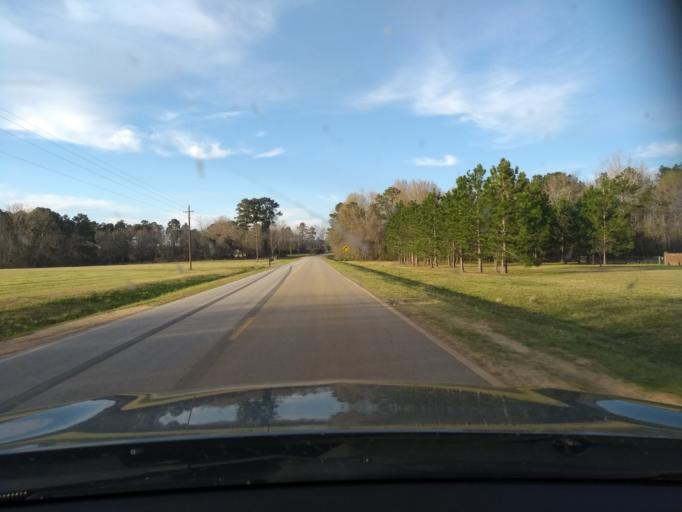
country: US
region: Georgia
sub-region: Bulloch County
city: Statesboro
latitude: 32.3399
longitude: -81.7735
